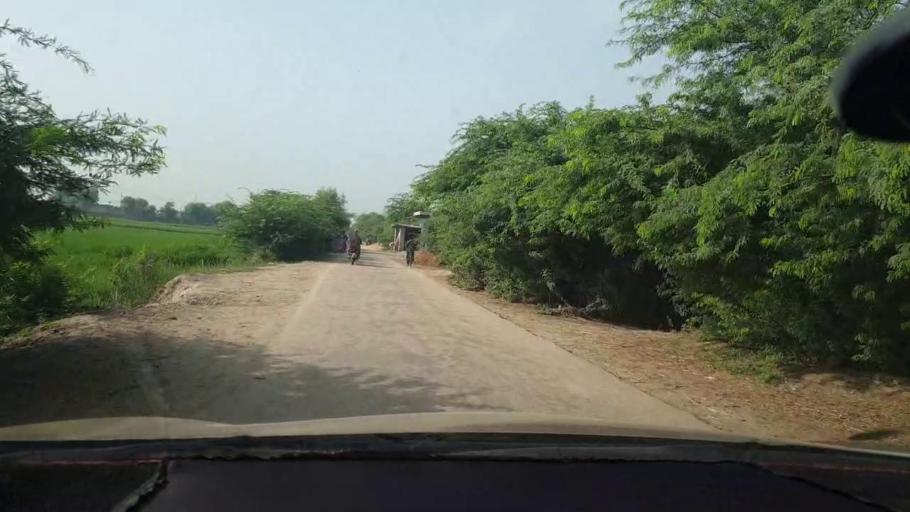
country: PK
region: Sindh
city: Kambar
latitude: 27.4999
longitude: 68.0121
